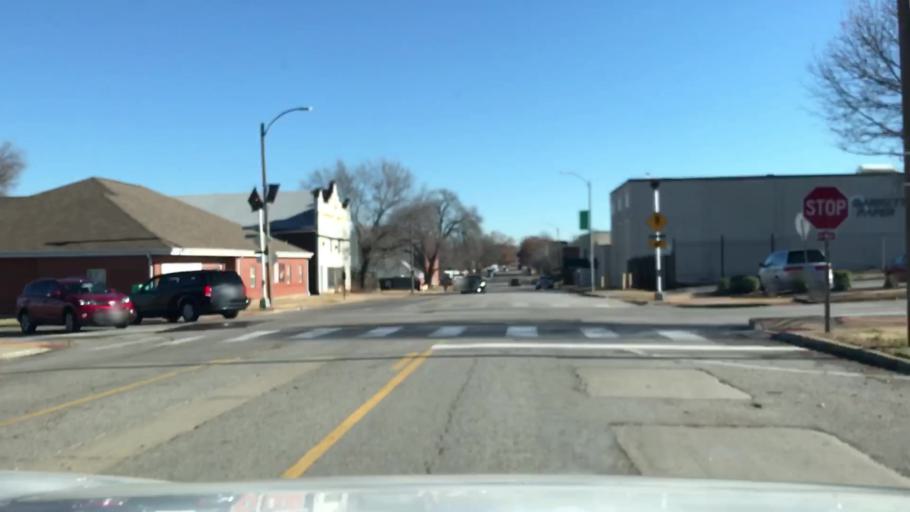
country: US
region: Missouri
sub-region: City of Saint Louis
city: St. Louis
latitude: 38.6198
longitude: -90.2319
